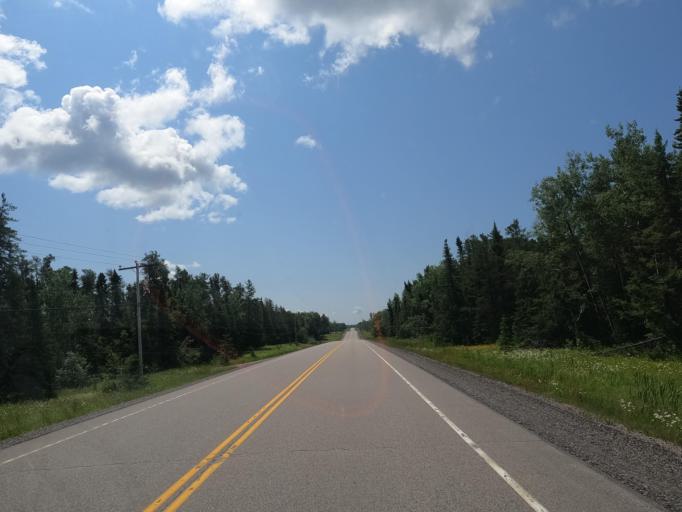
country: CA
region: Ontario
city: Dryden
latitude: 49.9206
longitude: -93.3597
